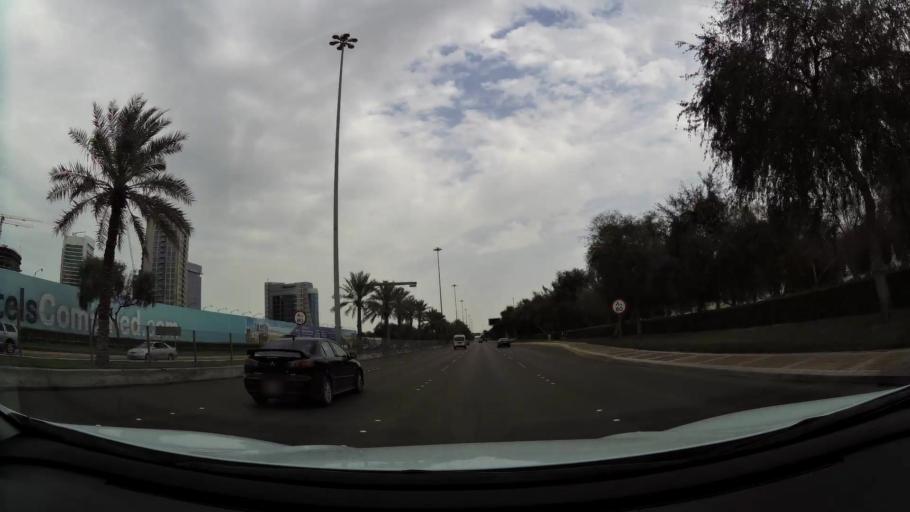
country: AE
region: Abu Dhabi
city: Abu Dhabi
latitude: 24.4280
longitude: 54.4335
